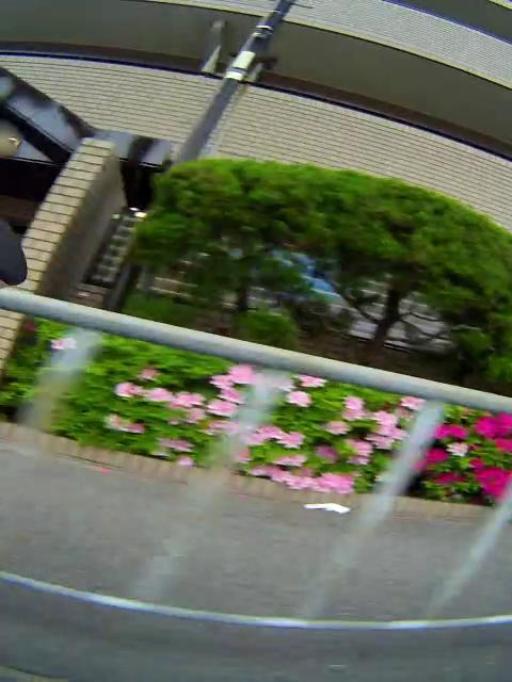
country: JP
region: Osaka
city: Mino
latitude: 34.8081
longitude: 135.4724
